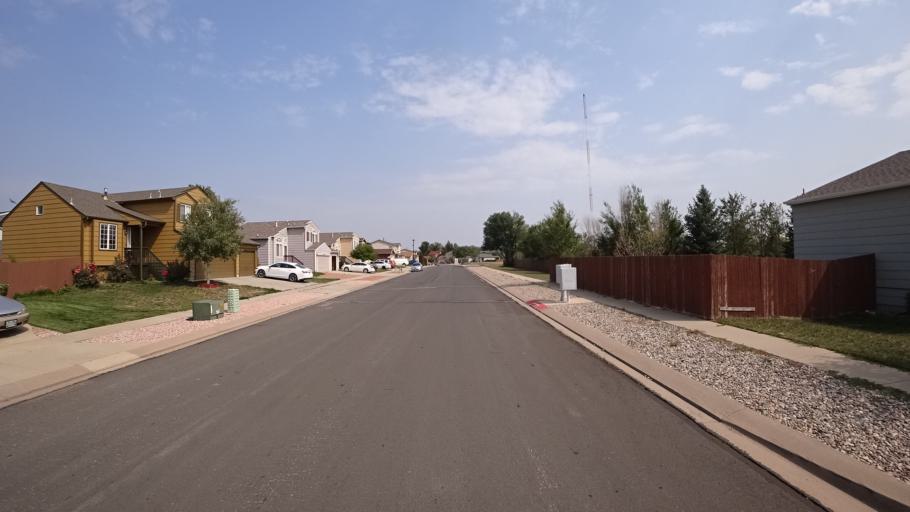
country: US
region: Colorado
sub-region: El Paso County
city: Cimarron Hills
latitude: 38.8269
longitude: -104.7430
